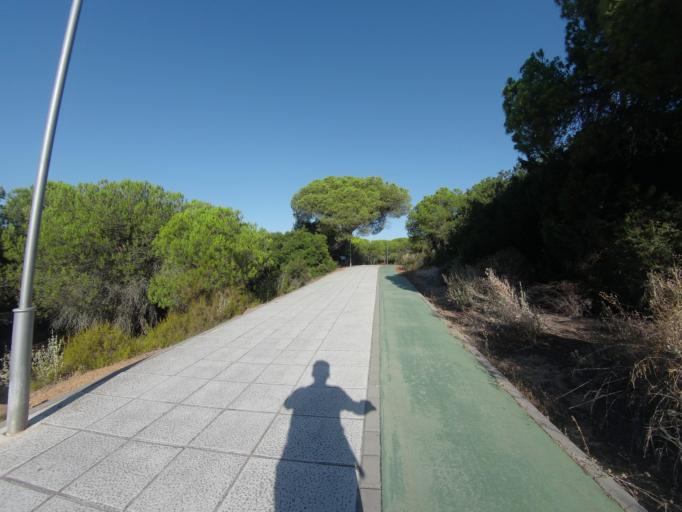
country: ES
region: Andalusia
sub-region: Provincia de Huelva
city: Aljaraque
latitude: 37.2128
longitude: -7.0673
